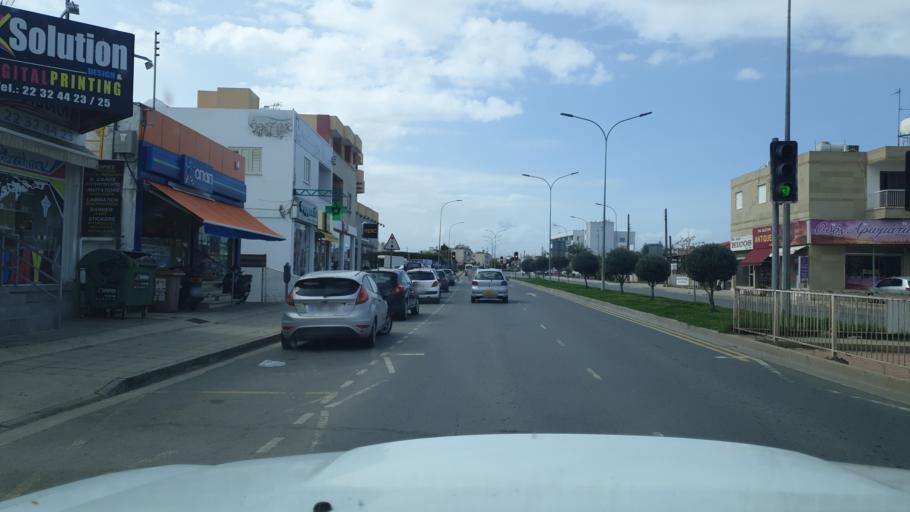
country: CY
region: Lefkosia
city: Tseri
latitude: 35.1216
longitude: 33.3192
